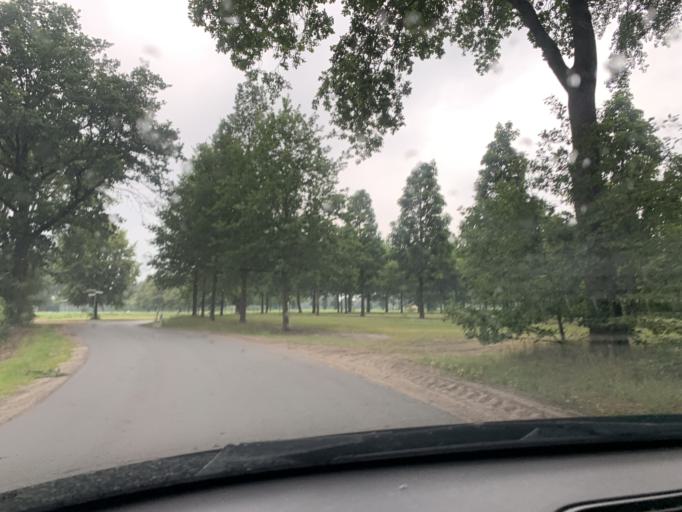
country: DE
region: Lower Saxony
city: Westerstede
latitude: 53.2372
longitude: 7.9673
